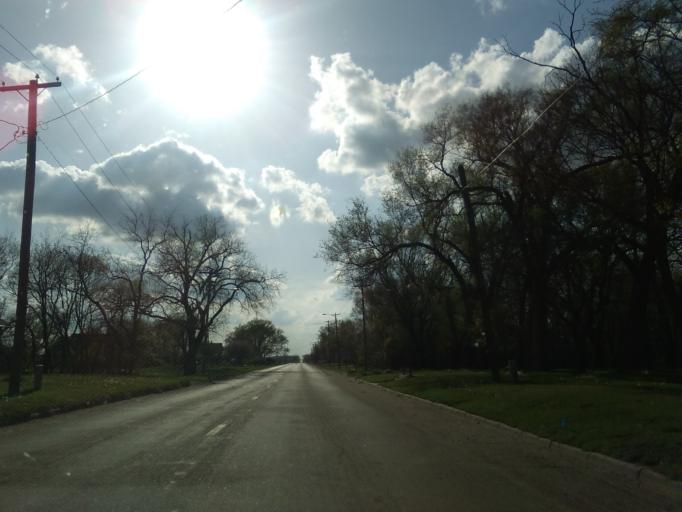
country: US
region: Nebraska
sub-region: Webster County
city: Red Cloud
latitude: 40.0888
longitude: -98.5288
